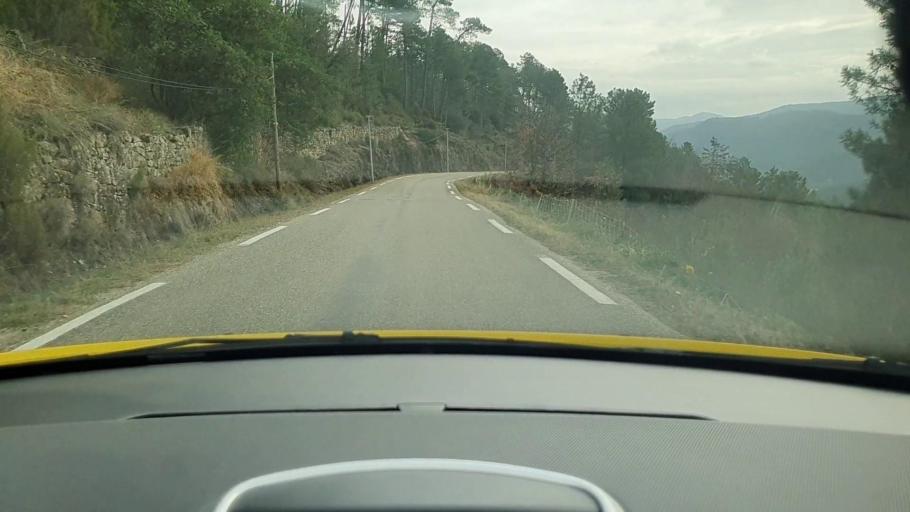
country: FR
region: Languedoc-Roussillon
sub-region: Departement du Gard
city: Besseges
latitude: 44.3085
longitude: 4.0799
